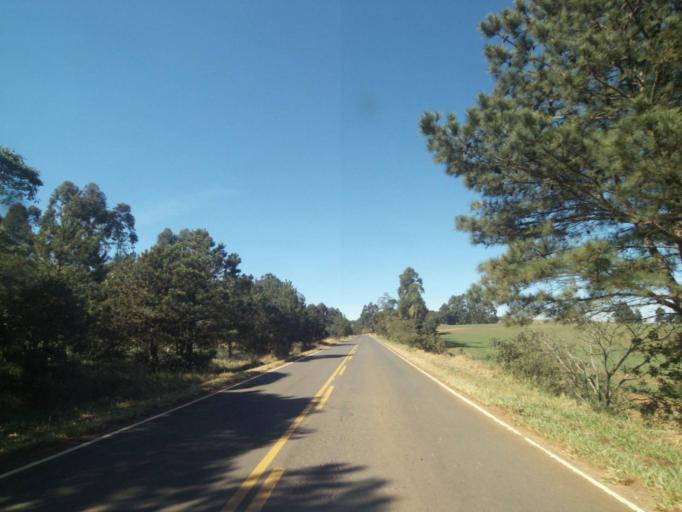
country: BR
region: Parana
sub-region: Tibagi
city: Tibagi
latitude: -24.4945
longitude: -50.4621
